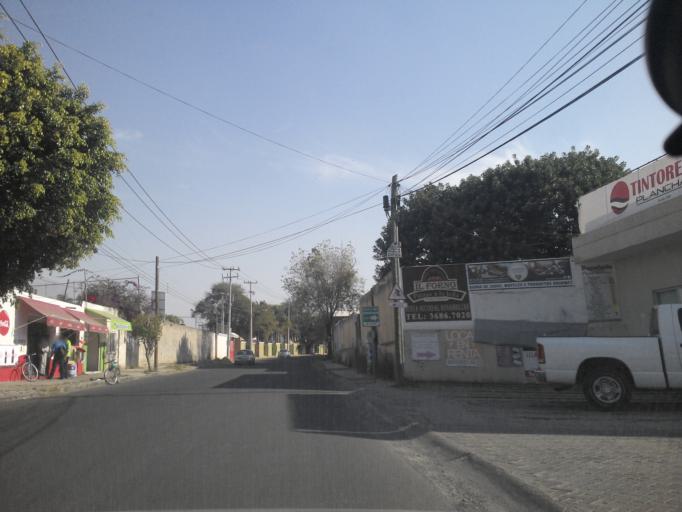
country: MX
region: Jalisco
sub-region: Tlajomulco de Zuniga
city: Palomar
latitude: 20.6124
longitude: -103.4538
